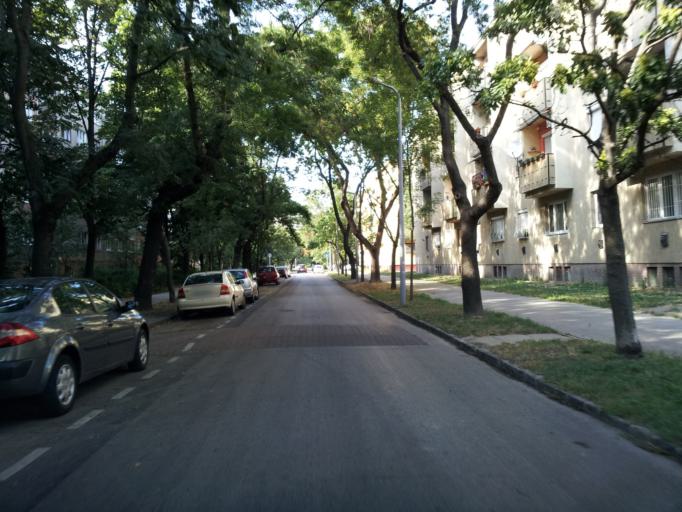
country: HU
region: Budapest
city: Budapest III. keruelet
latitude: 47.5410
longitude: 19.0355
